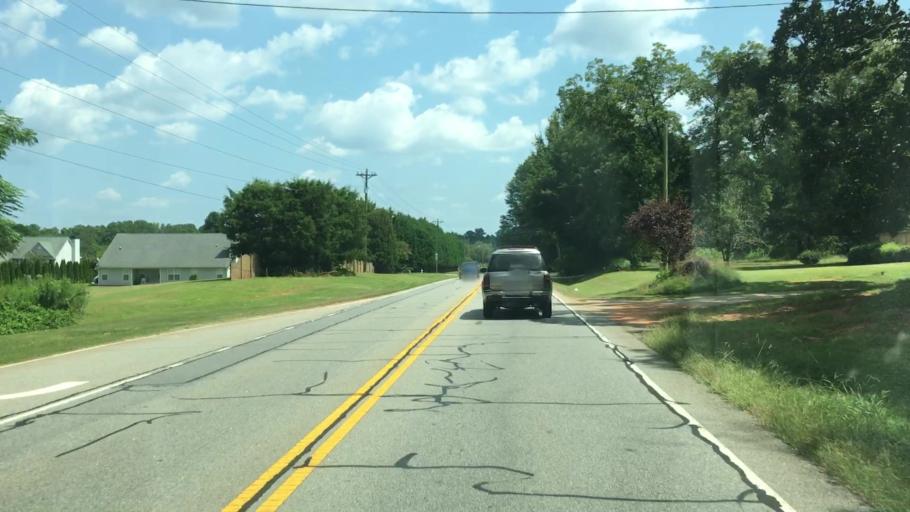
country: US
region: Georgia
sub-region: Oconee County
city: Bogart
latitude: 33.8958
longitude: -83.5704
